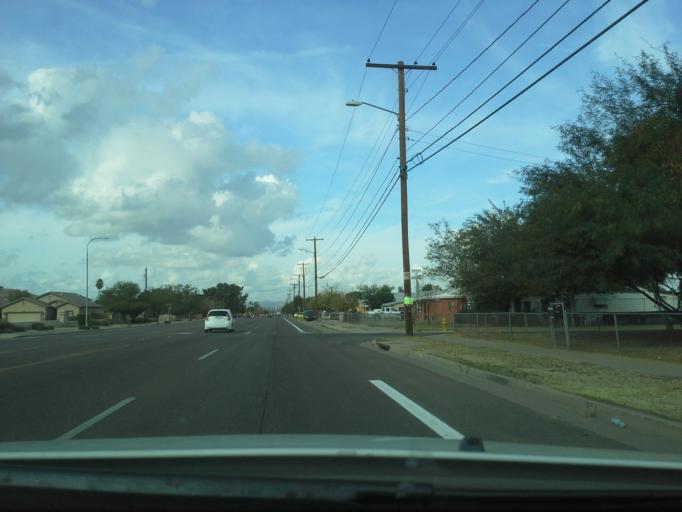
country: US
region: Arizona
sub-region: Maricopa County
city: Phoenix
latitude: 33.3865
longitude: -112.0819
